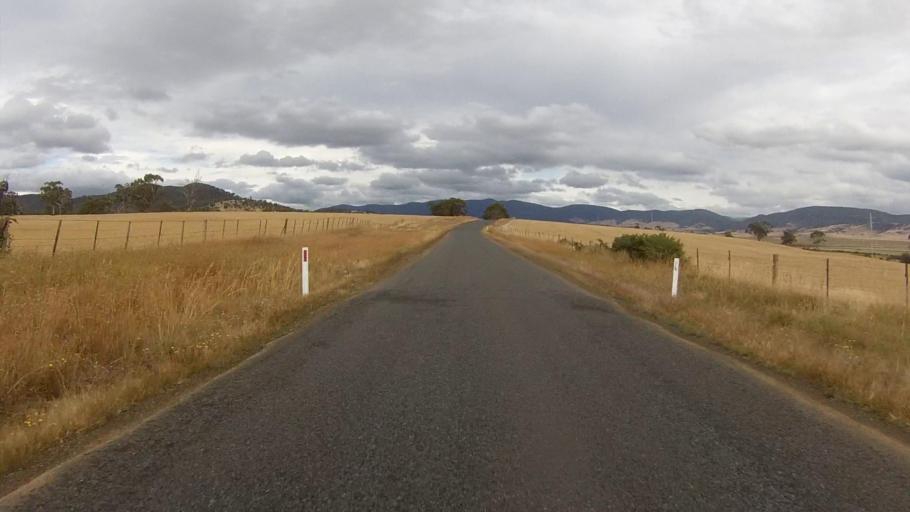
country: AU
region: Tasmania
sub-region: Northern Midlands
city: Evandale
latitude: -41.7925
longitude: 147.7435
